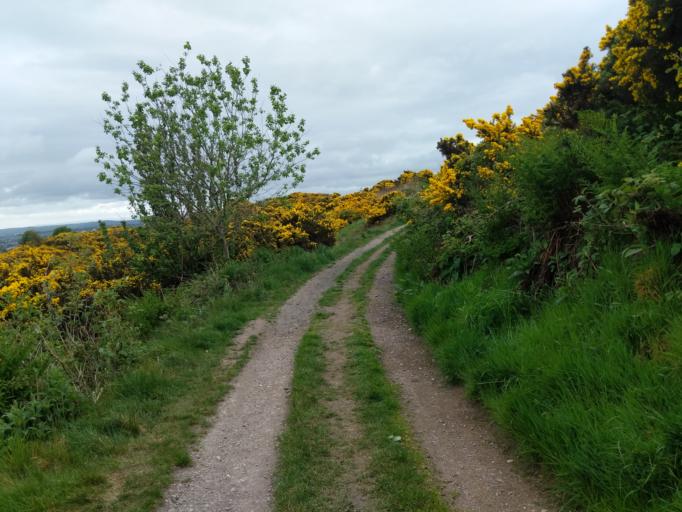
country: GB
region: Scotland
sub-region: Edinburgh
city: Edinburgh
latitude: 55.9168
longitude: -3.1966
